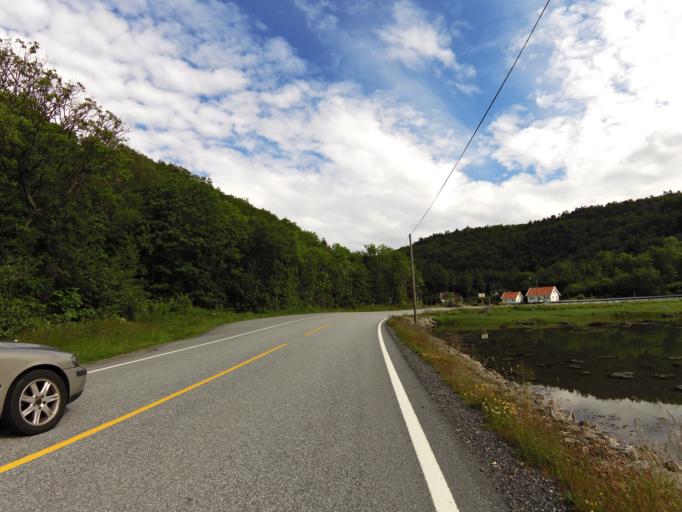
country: NO
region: Vest-Agder
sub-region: Lindesnes
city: Vigeland
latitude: 58.0584
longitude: 7.1781
